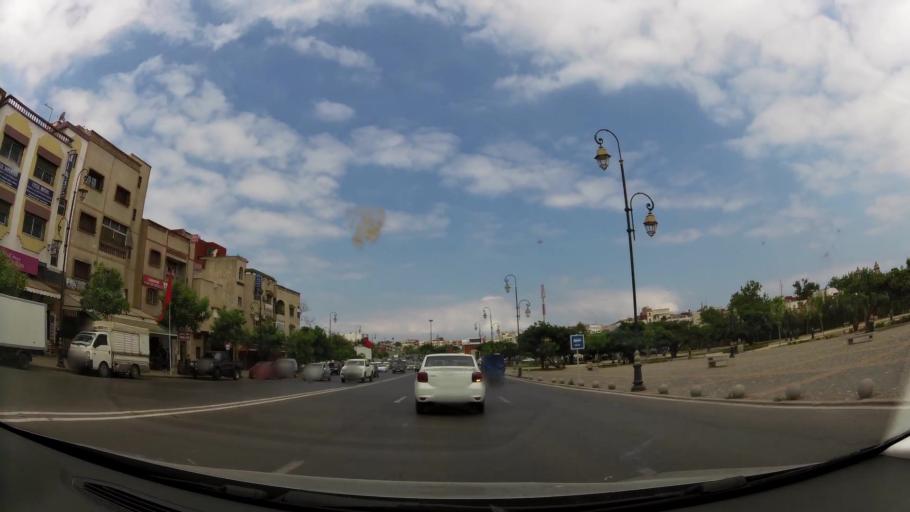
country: MA
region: Rabat-Sale-Zemmour-Zaer
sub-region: Skhirate-Temara
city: Temara
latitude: 33.9757
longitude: -6.8859
